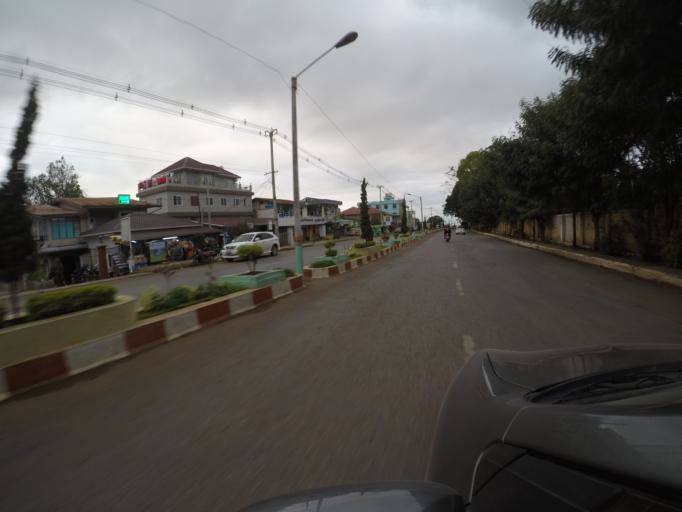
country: MM
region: Shan
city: Taunggyi
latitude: 20.8054
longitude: 97.0369
